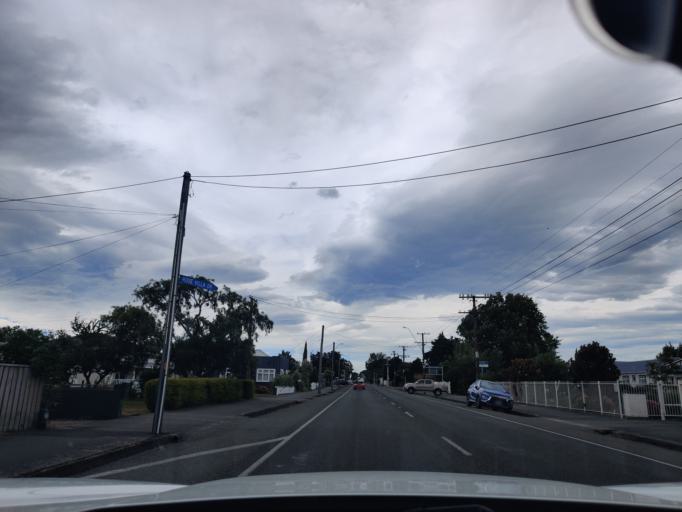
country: NZ
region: Wellington
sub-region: Masterton District
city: Masterton
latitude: -41.0318
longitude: 175.5209
